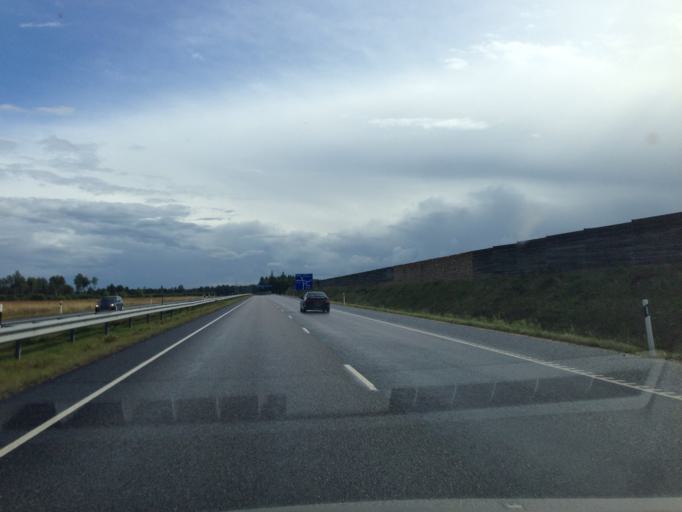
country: EE
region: Jaervamaa
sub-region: Paide linn
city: Paide
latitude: 58.9081
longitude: 25.6282
